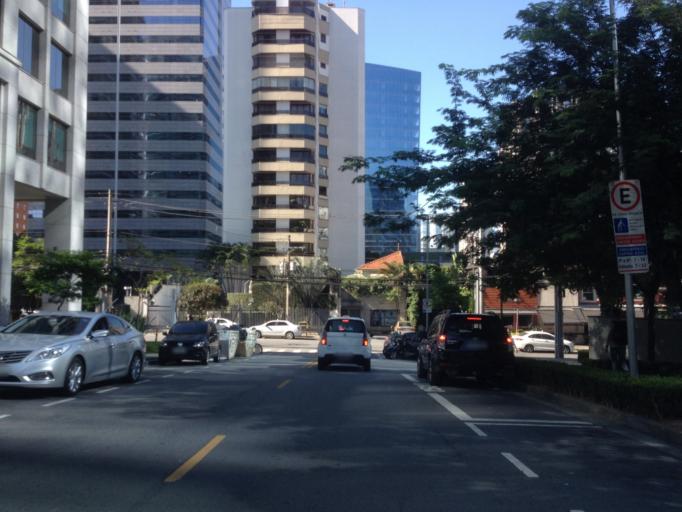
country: BR
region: Sao Paulo
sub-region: Sao Paulo
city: Sao Paulo
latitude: -23.5868
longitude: -46.6811
